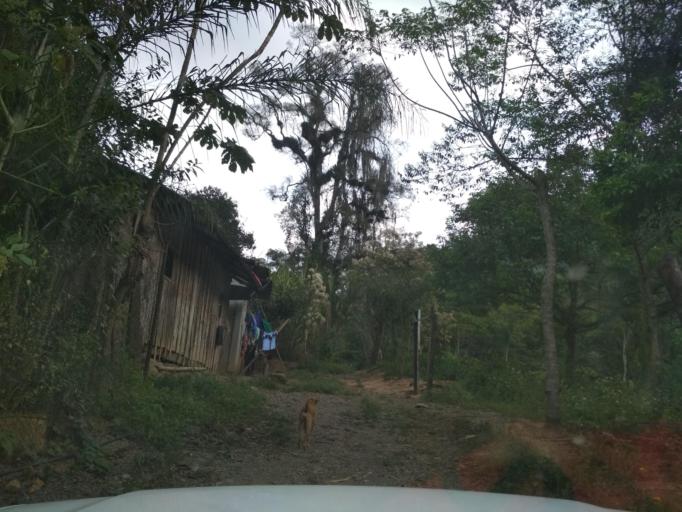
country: MX
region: Veracruz
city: Cuautlapan
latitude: 18.8682
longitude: -97.0103
